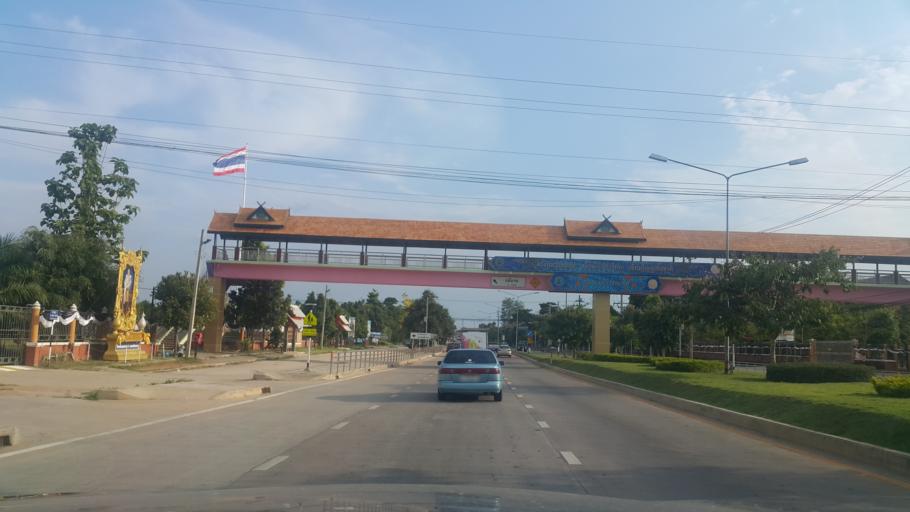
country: TH
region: Chiang Rai
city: Chiang Rai
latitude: 19.9290
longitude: 99.8636
